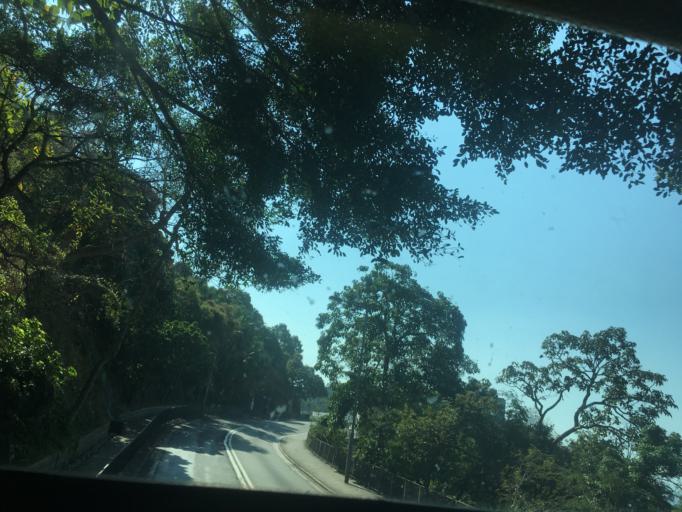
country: HK
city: Hong Kong
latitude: 22.2768
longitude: 114.1173
